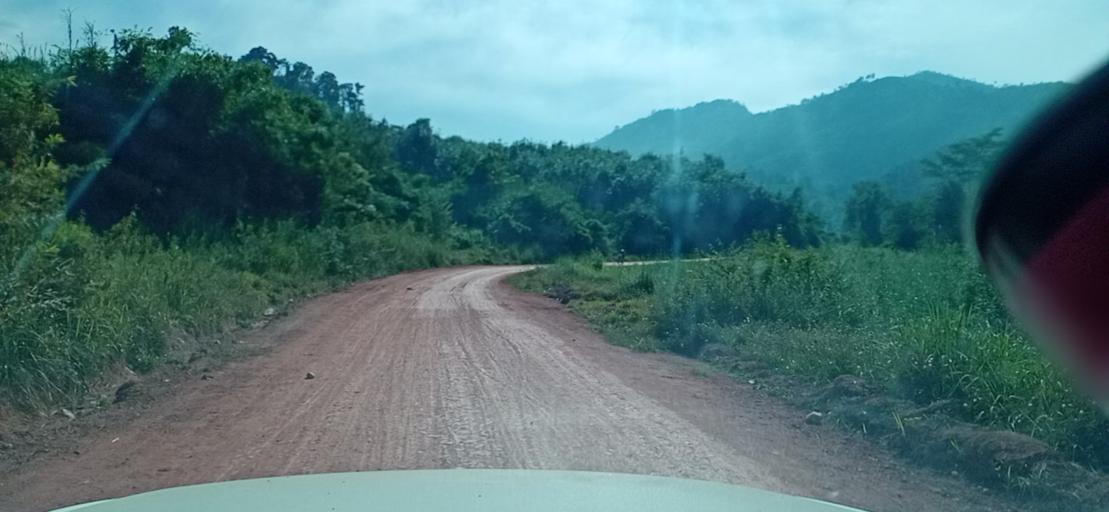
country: TH
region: Changwat Bueng Kan
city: Pak Khat
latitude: 18.6698
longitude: 103.2001
